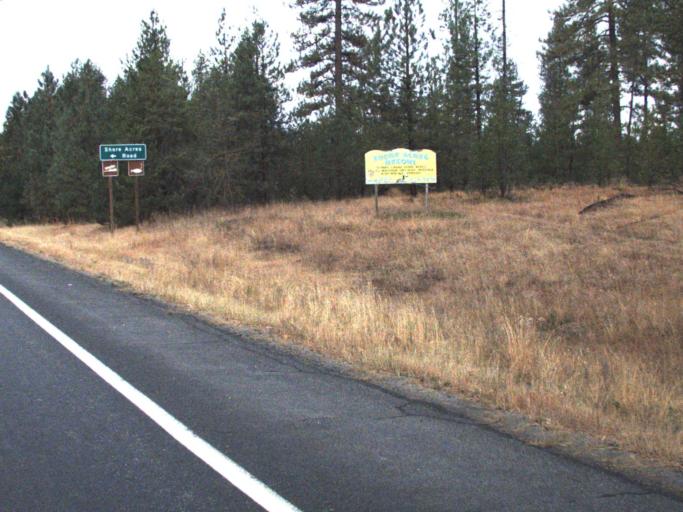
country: US
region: Washington
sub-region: Spokane County
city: Deer Park
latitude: 48.0645
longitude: -117.6554
